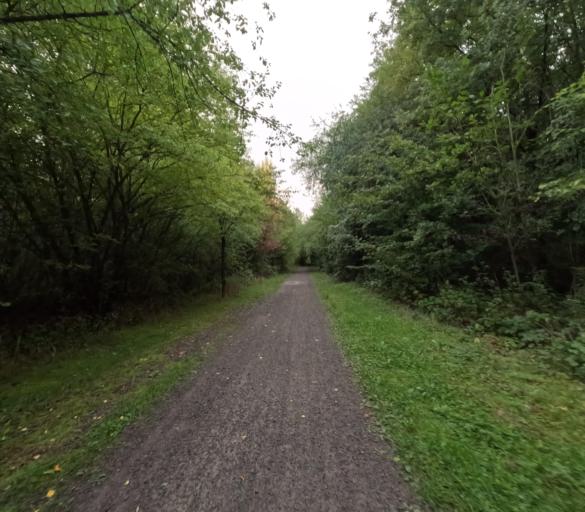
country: DE
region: Saxony
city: Markranstadt
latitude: 51.2918
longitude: 12.2280
